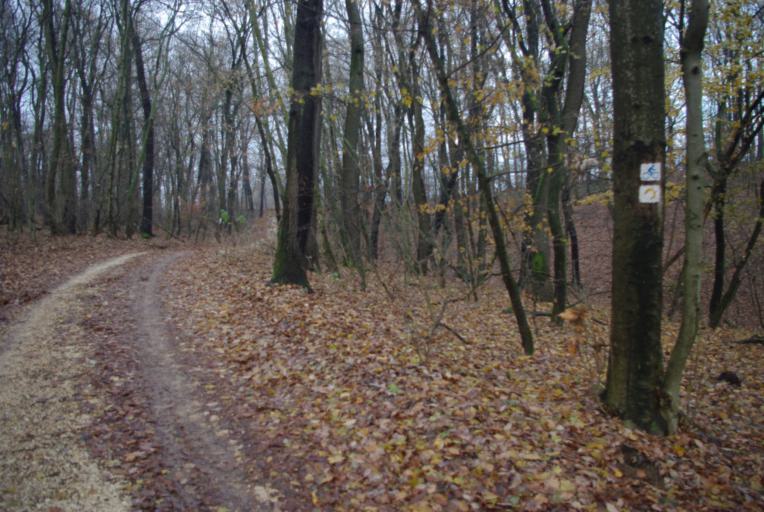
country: HU
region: Pest
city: Piliscsaba
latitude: 47.6435
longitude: 18.8514
